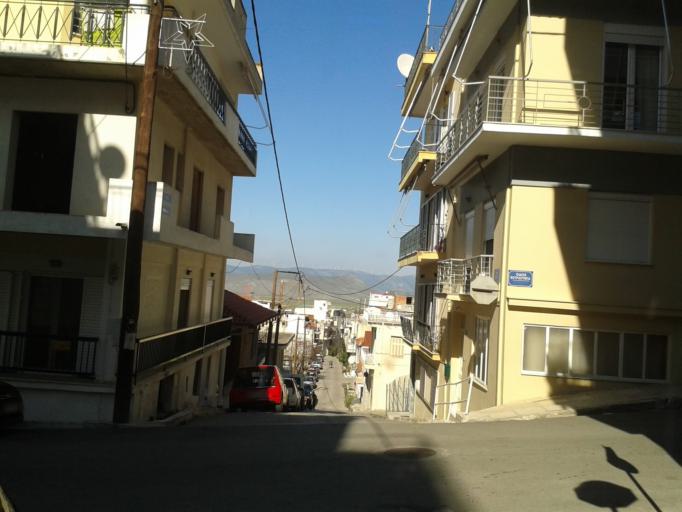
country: GR
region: Central Greece
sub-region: Nomos Voiotias
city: Thivai
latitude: 38.3213
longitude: 23.3164
